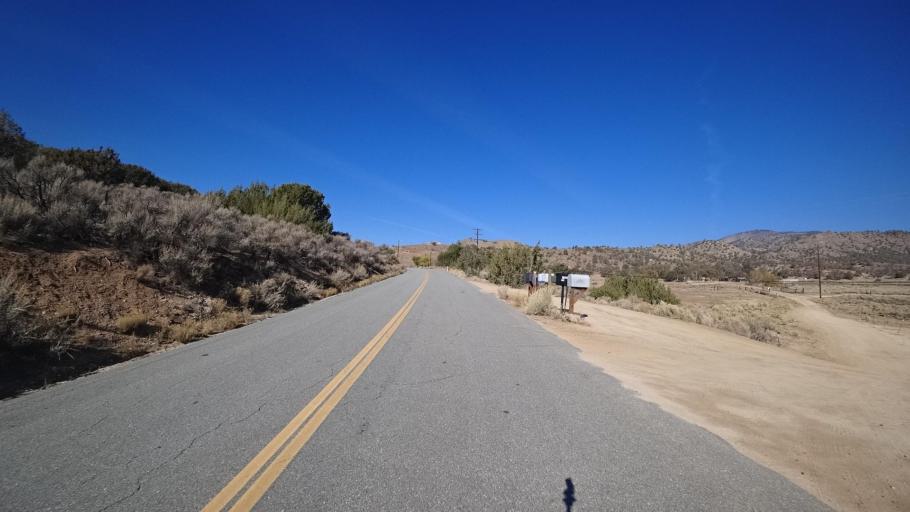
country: US
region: California
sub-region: Kern County
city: Tehachapi
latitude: 35.3667
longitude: -118.3853
